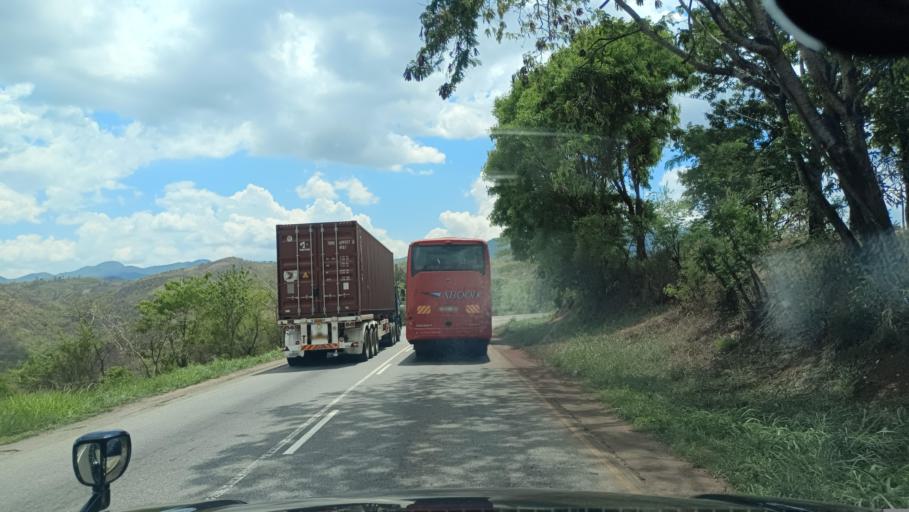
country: TZ
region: Morogoro
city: Mikumi
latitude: -7.4642
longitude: 36.9187
